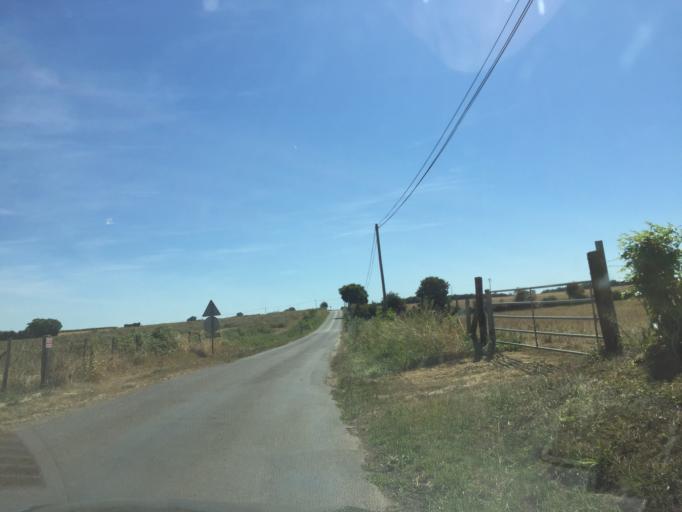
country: FR
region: Poitou-Charentes
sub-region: Departement de la Vienne
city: Vivonne
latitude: 46.4378
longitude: 0.3090
